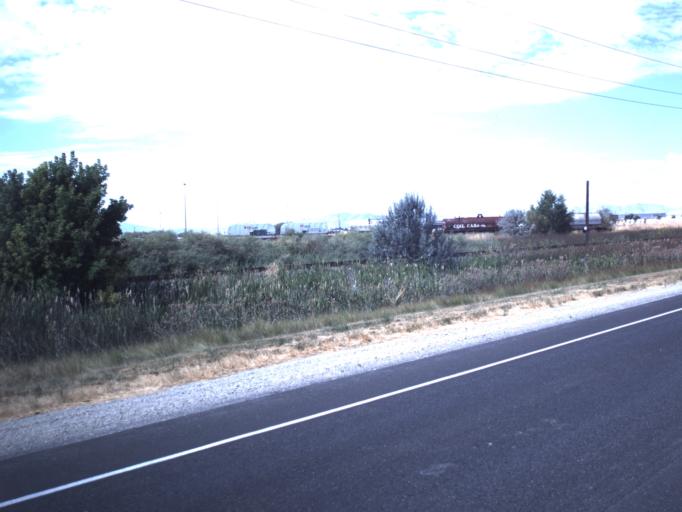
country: US
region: Utah
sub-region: Box Elder County
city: Brigham City
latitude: 41.5313
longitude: -112.0452
